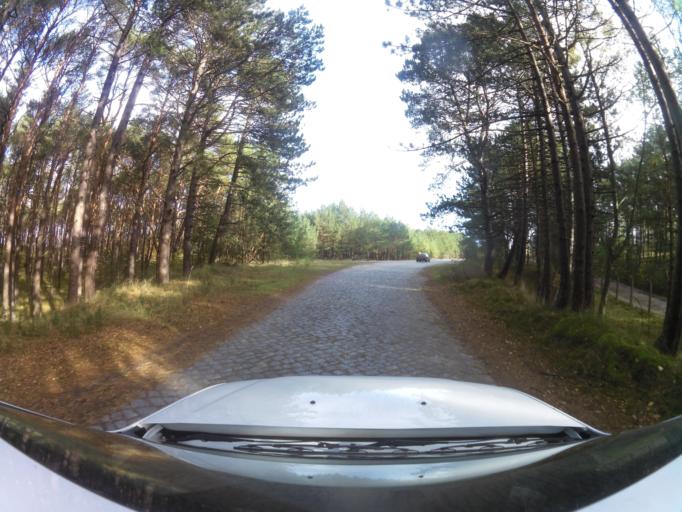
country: PL
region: West Pomeranian Voivodeship
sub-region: Powiat gryficki
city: Trzebiatow
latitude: 54.1180
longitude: 15.1783
